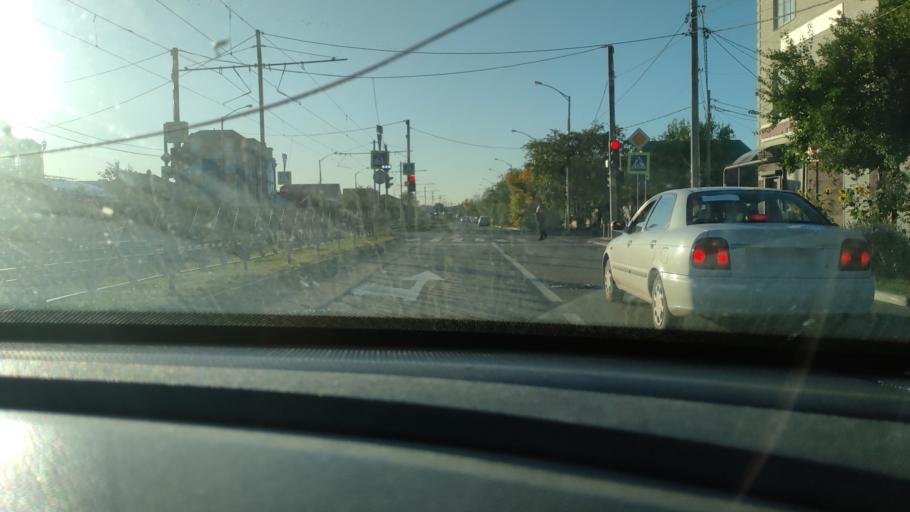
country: RU
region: Krasnodarskiy
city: Krasnodar
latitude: 45.0425
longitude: 38.9412
